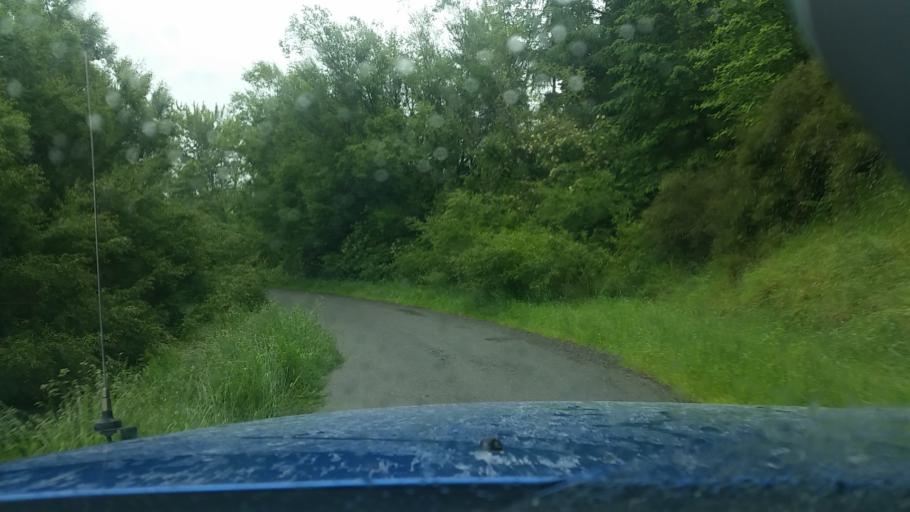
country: NZ
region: Canterbury
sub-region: Ashburton District
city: Methven
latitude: -43.7146
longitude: 171.3210
